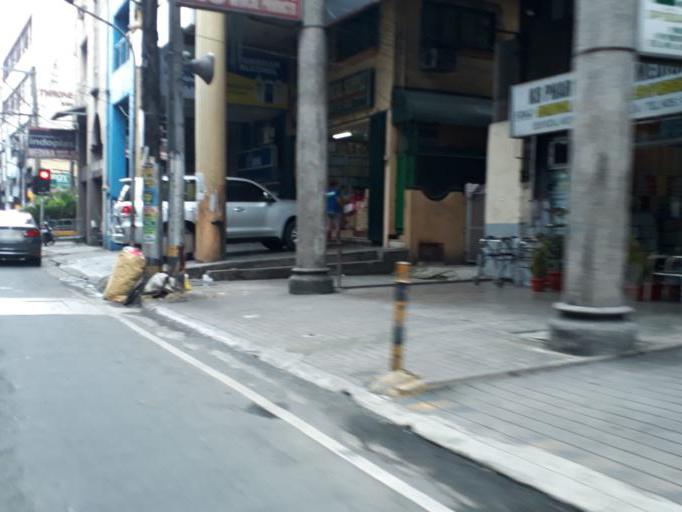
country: PH
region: Metro Manila
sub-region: City of Manila
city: Manila
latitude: 14.6127
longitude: 120.9827
